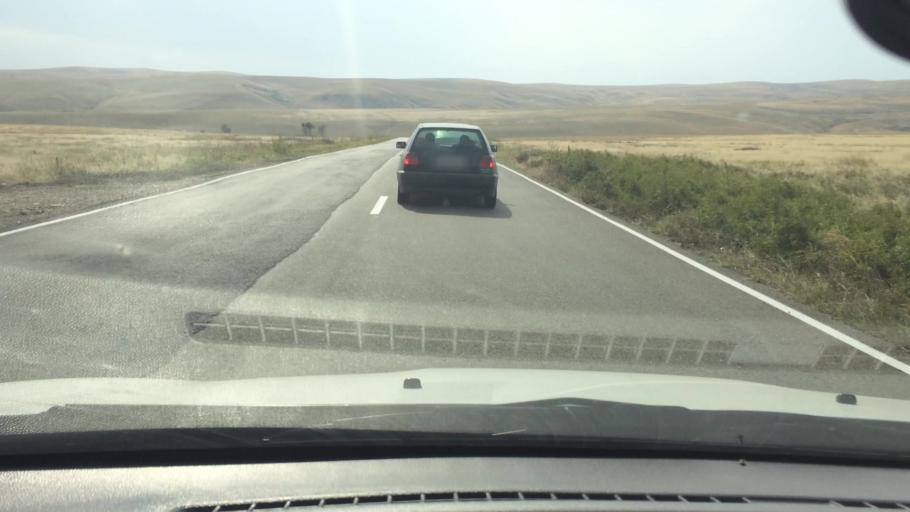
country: GE
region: Kvemo Kartli
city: Rust'avi
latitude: 41.5306
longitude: 44.9409
